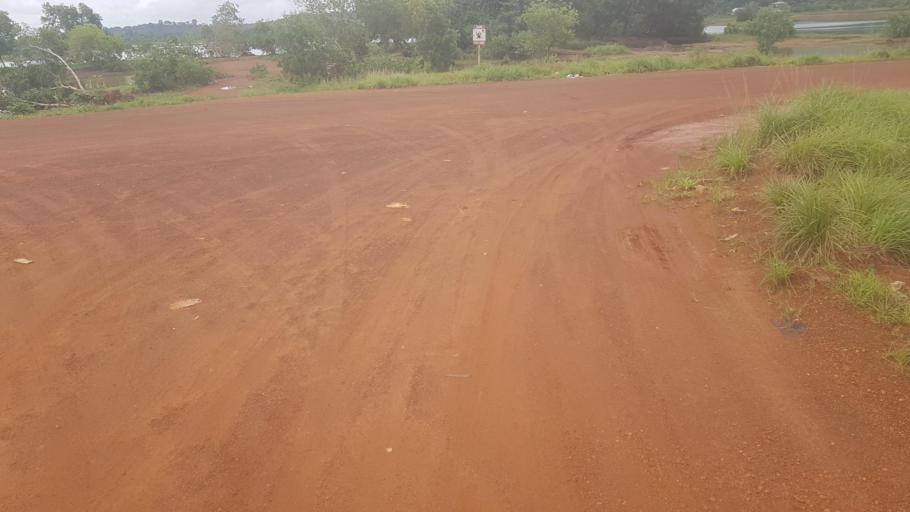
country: SL
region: Southern Province
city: Mogbwemo
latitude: 7.7570
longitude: -12.3044
